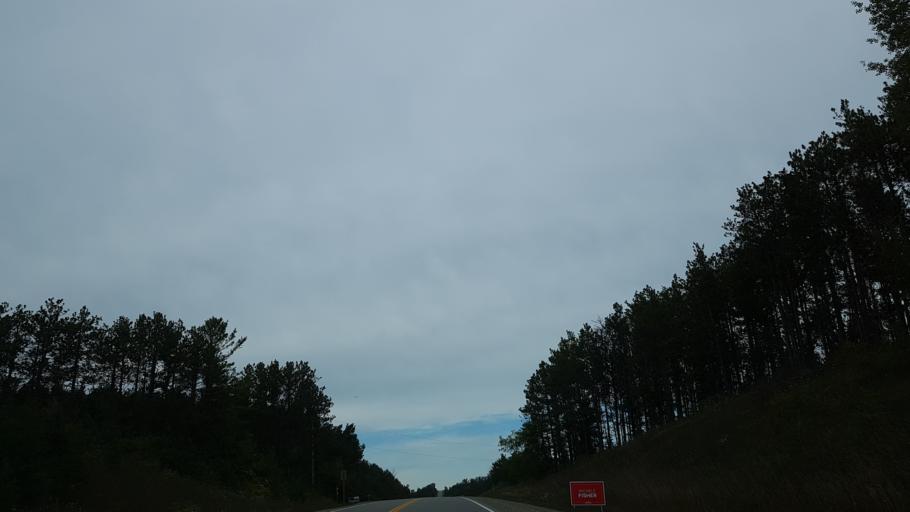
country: CA
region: Ontario
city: Orangeville
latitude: 44.0800
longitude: -80.0186
